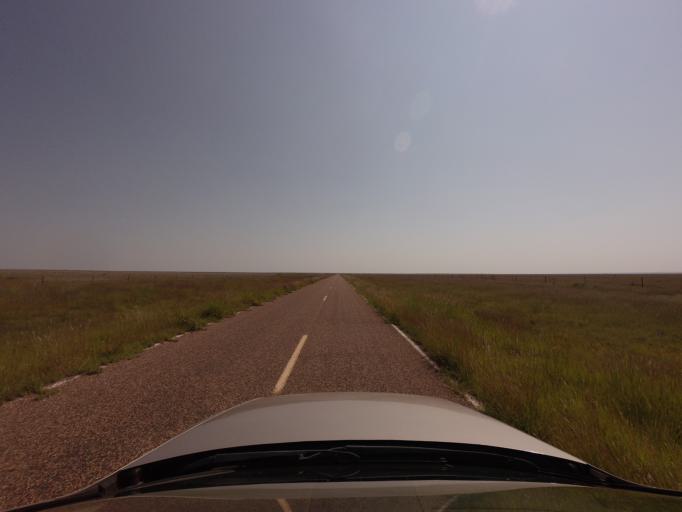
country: US
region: New Mexico
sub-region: Curry County
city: Cannon Air Force Base
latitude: 34.6333
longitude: -103.4308
